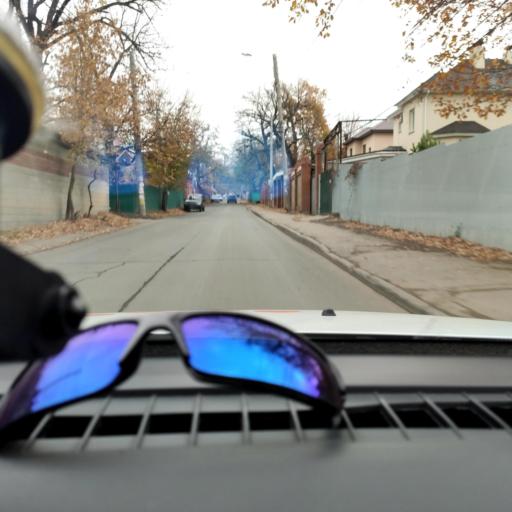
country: RU
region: Samara
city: Samara
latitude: 53.2557
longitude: 50.1901
